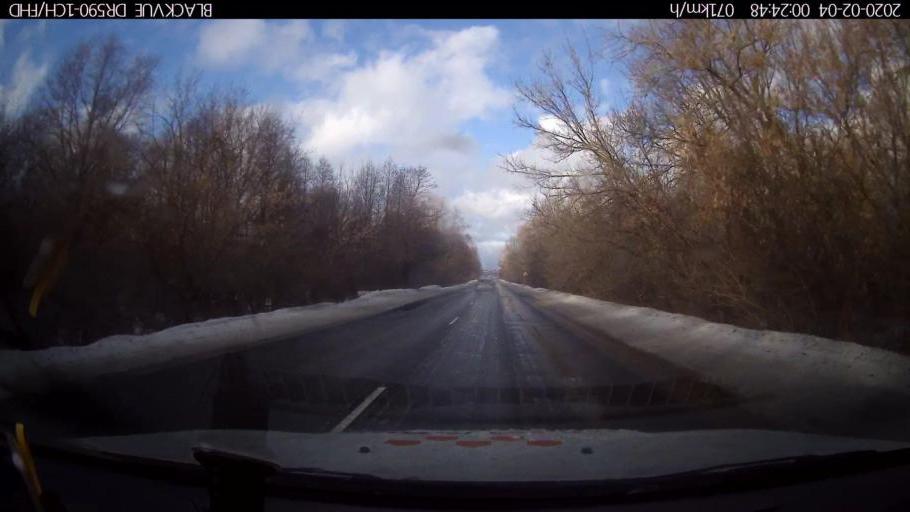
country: RU
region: Nizjnij Novgorod
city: Kstovo
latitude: 55.9990
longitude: 44.2117
